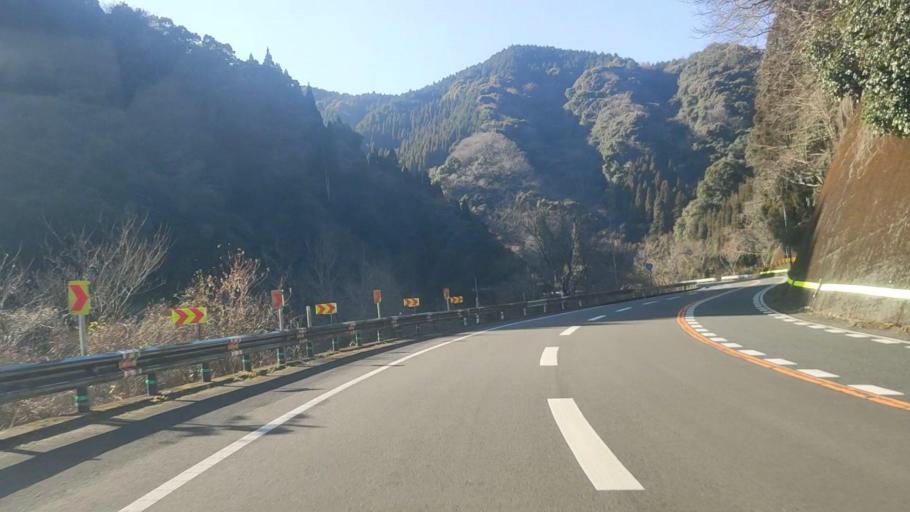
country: JP
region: Oita
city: Tsukumiura
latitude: 32.9987
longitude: 131.7840
